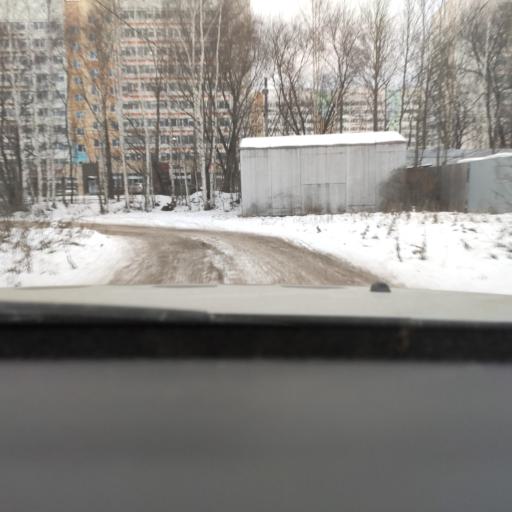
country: RU
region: Perm
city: Perm
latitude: 58.0491
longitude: 56.3491
